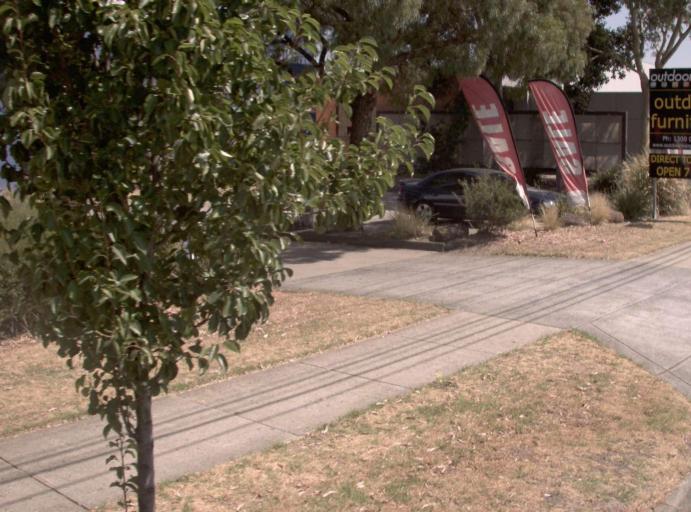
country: AU
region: Victoria
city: Heatherton
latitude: -37.9576
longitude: 145.0759
